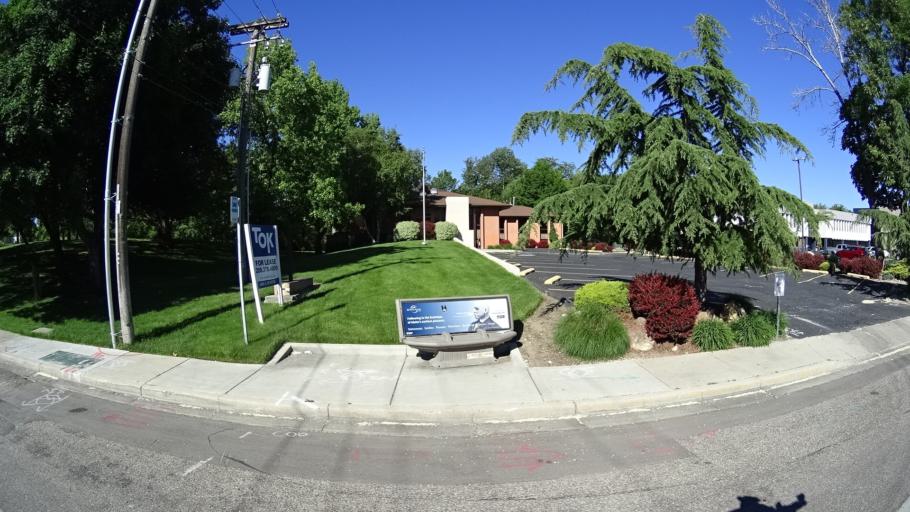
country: US
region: Idaho
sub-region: Ada County
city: Boise
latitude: 43.6149
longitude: -116.2191
